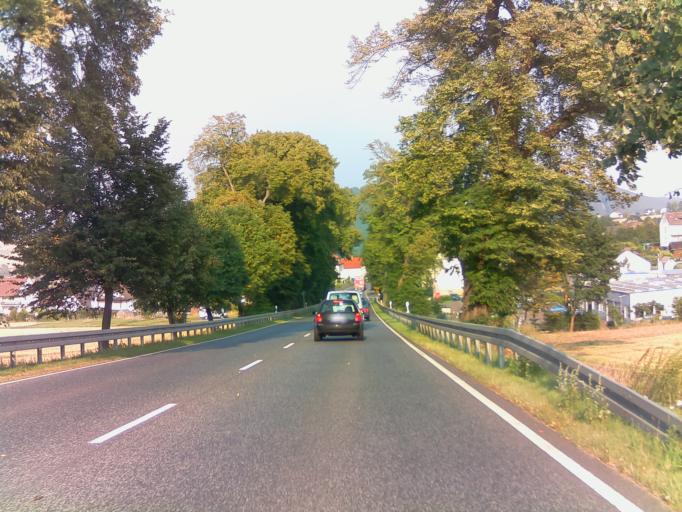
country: DE
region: Hesse
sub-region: Regierungsbezirk Kassel
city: Bad Hersfeld
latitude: 50.8681
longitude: 9.7503
